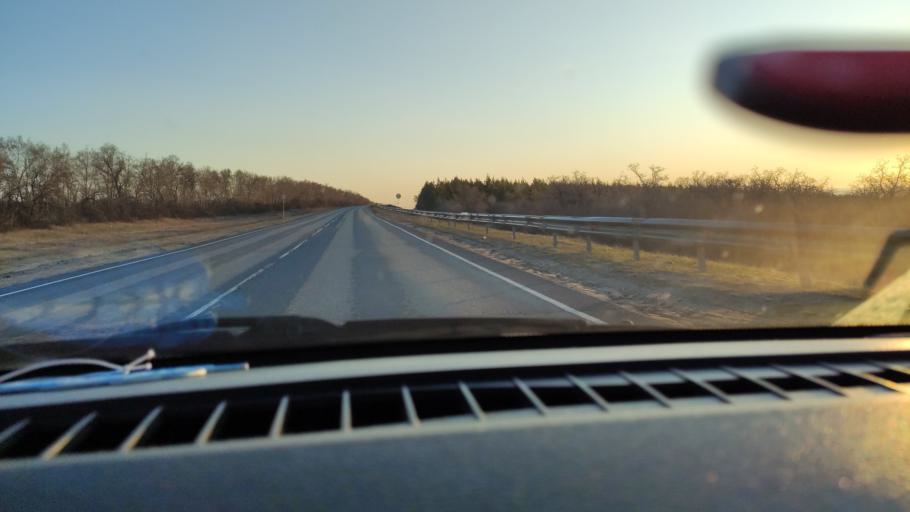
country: RU
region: Saratov
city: Sinodskoye
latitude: 51.9393
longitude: 46.5949
